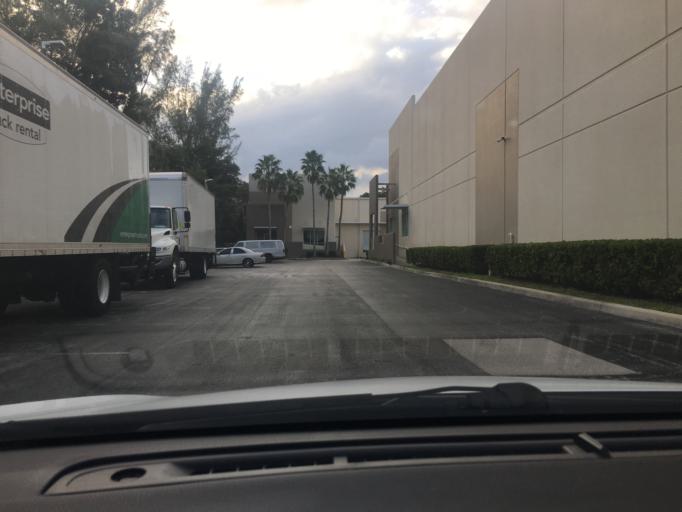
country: US
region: Florida
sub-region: Broward County
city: Dania Beach
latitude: 26.0684
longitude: -80.1795
